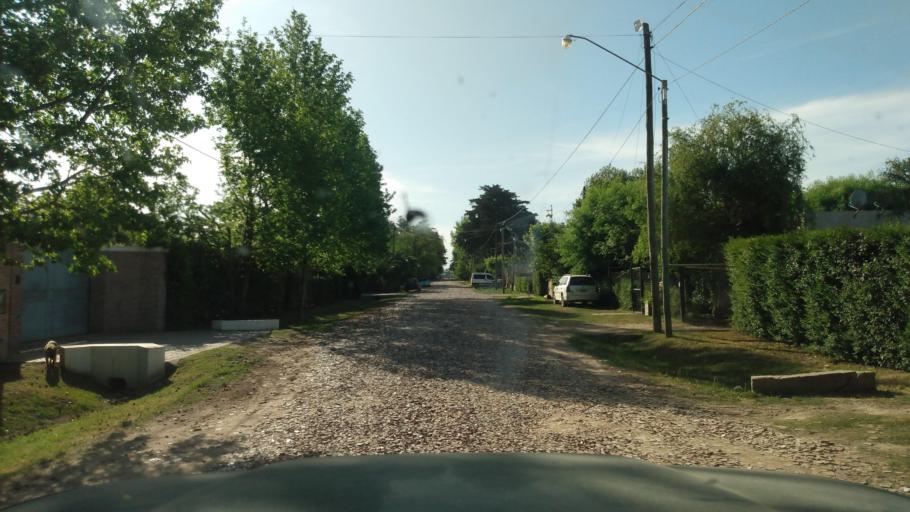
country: AR
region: Buenos Aires
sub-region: Partido de Lujan
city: Lujan
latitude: -34.5937
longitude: -59.1400
